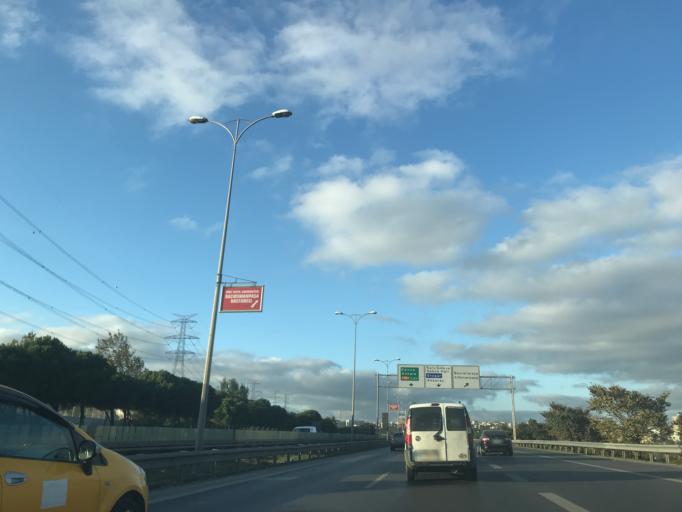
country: TR
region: Istanbul
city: Esenler
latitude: 41.0521
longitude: 28.8857
